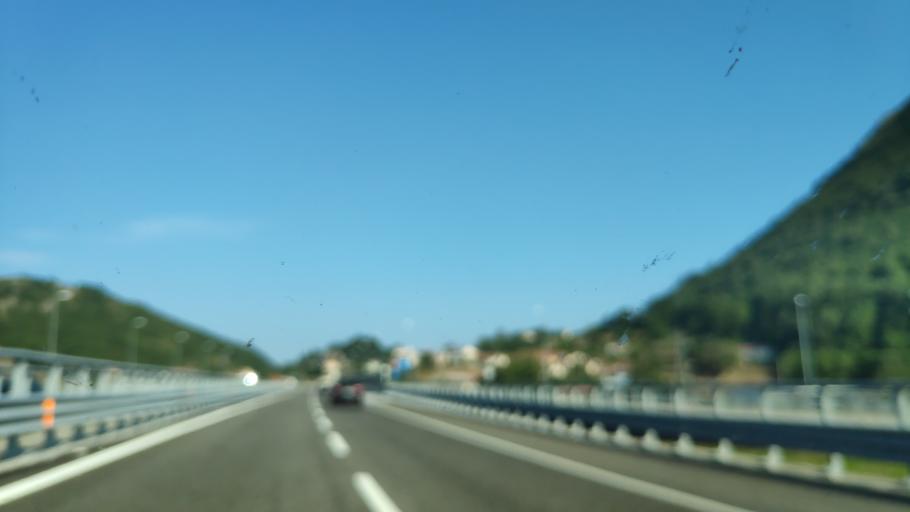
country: IT
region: Basilicate
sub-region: Provincia di Potenza
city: Lauria
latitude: 40.0183
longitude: 15.8875
